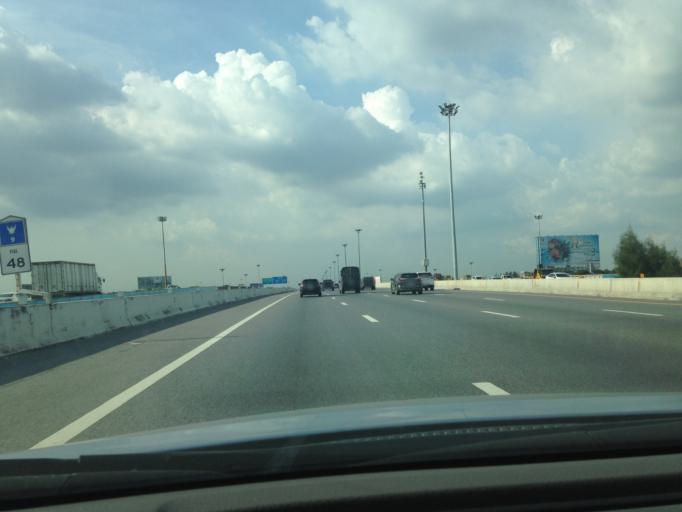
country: TH
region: Bangkok
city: Saphan Sung
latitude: 13.7824
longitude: 100.6853
